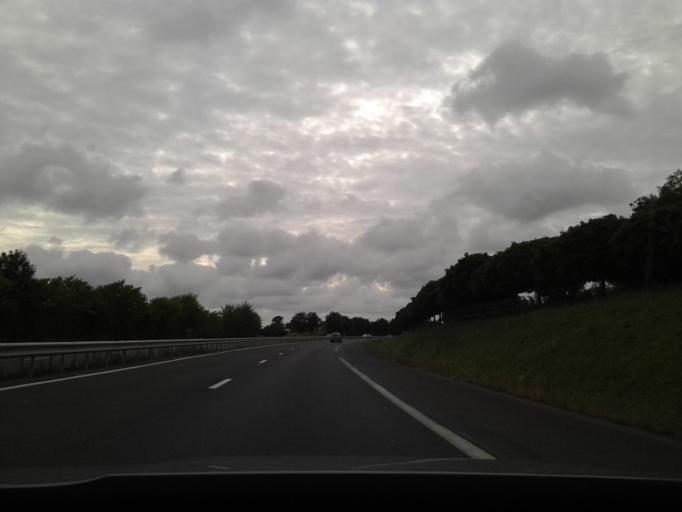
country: FR
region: Lower Normandy
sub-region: Departement du Calvados
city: Grandcamp-Maisy
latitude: 49.3435
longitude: -1.0241
